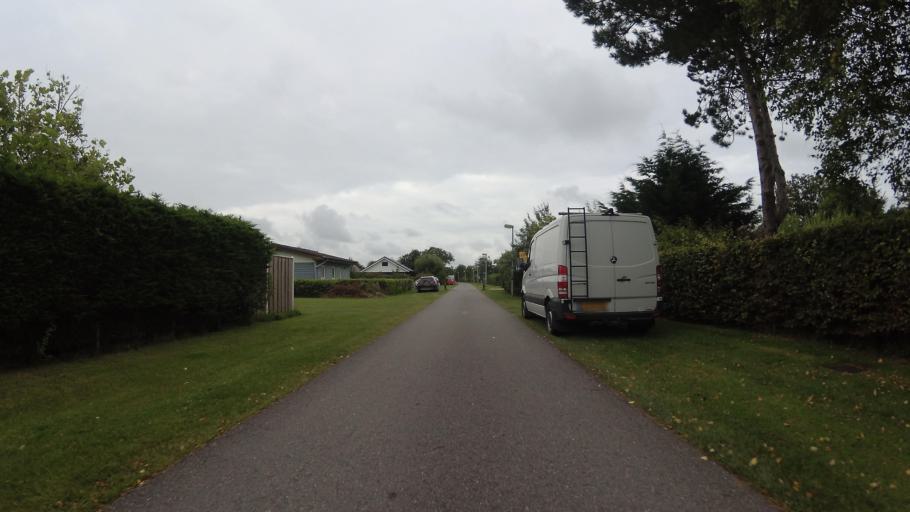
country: NL
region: North Holland
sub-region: Gemeente Den Helder
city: Den Helder
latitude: 52.8982
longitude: 4.7304
